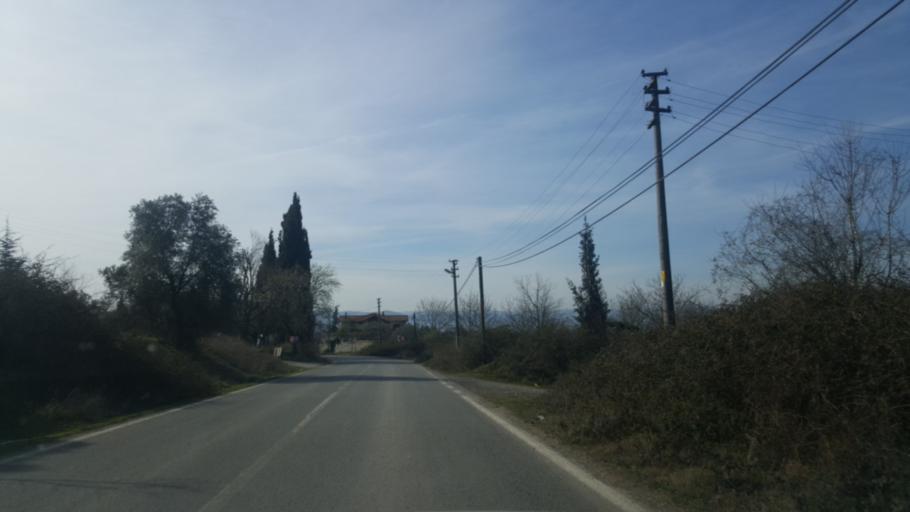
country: TR
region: Kocaeli
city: Tavsancil
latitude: 40.7790
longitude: 29.5750
